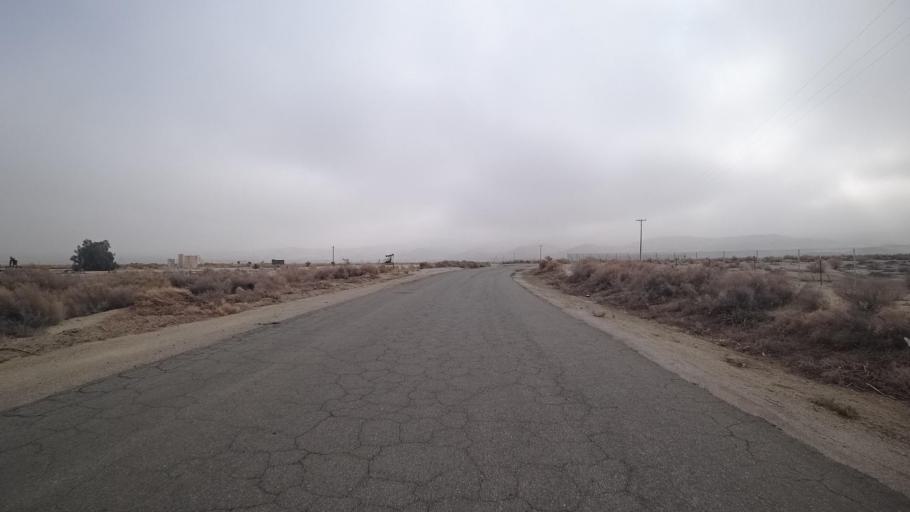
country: US
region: California
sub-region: Kern County
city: Maricopa
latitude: 35.0526
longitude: -119.3938
